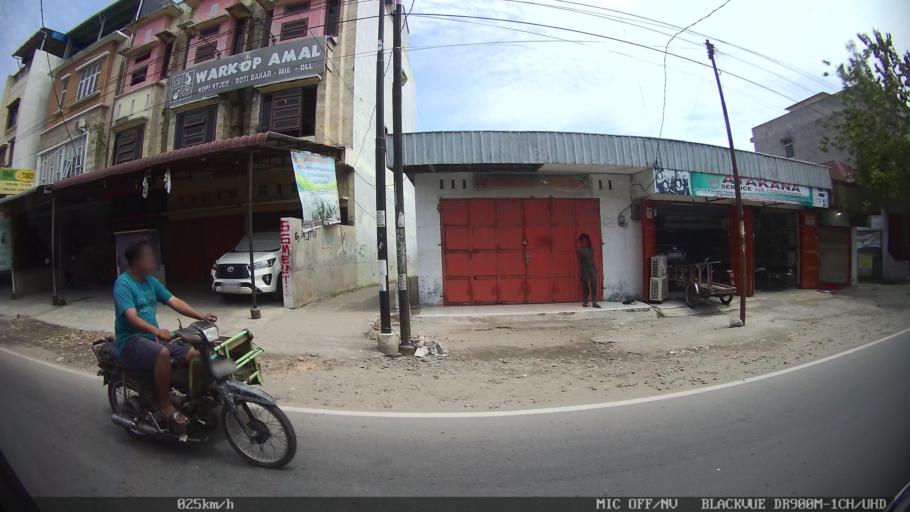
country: ID
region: North Sumatra
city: Sunggal
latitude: 3.5856
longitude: 98.6187
